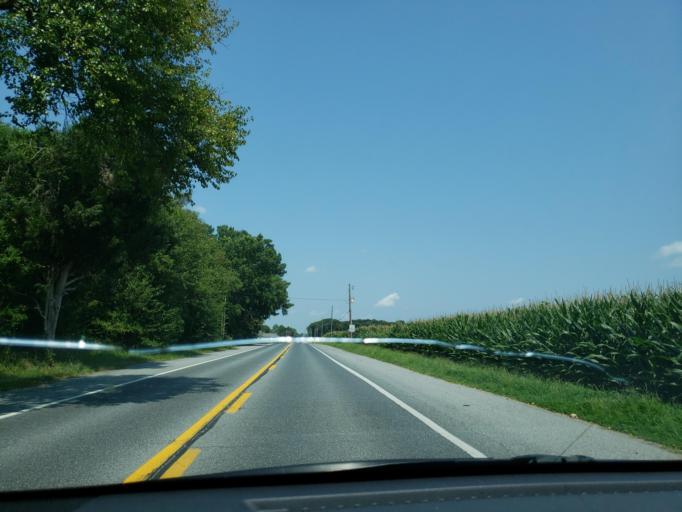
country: US
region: Delaware
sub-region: Sussex County
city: Milton
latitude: 38.7940
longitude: -75.3140
